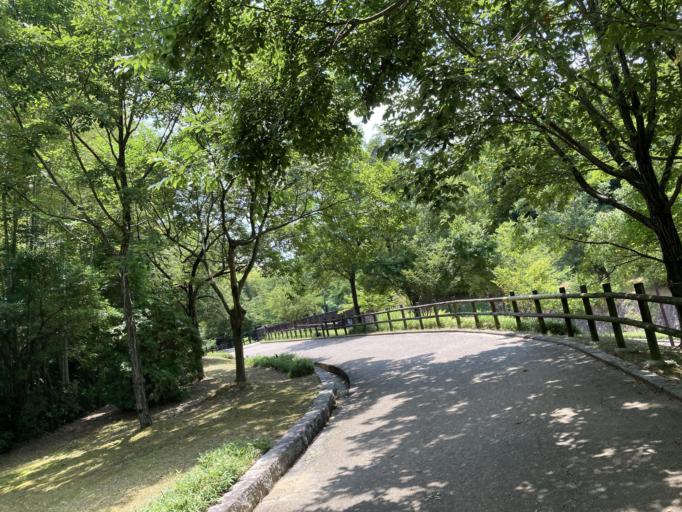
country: JP
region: Nara
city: Tawaramoto
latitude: 34.5733
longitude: 135.7377
